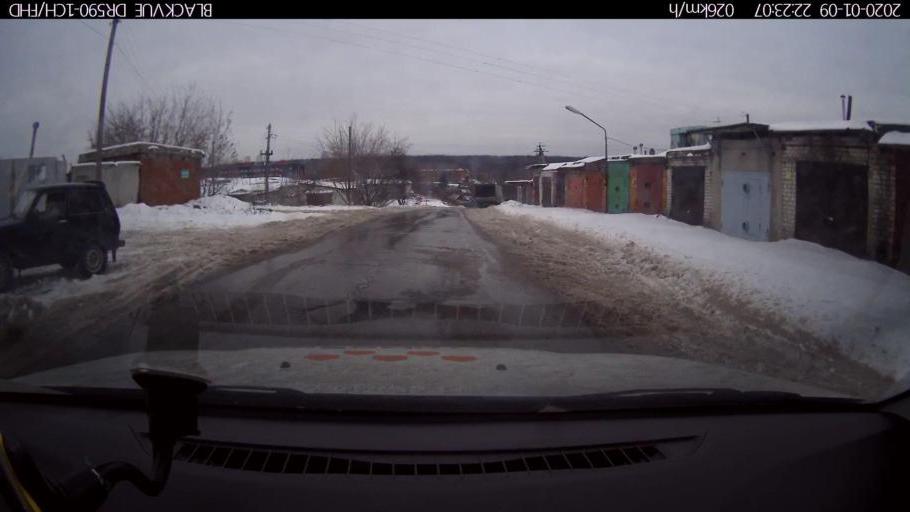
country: RU
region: Nizjnij Novgorod
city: Afonino
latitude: 56.2395
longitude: 44.0091
